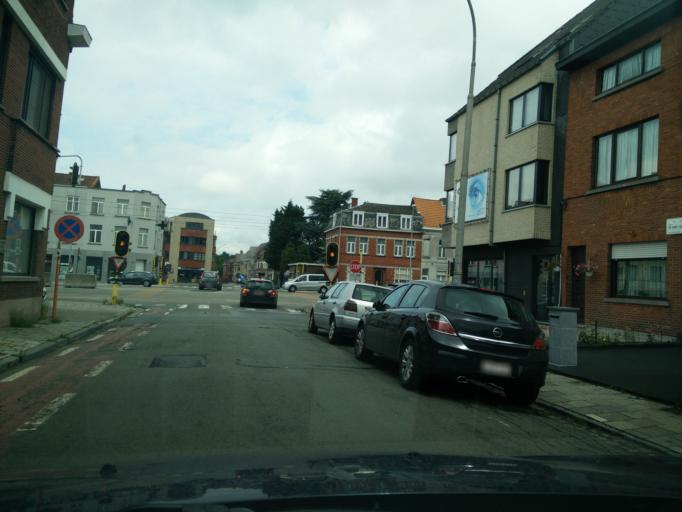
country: BE
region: Flanders
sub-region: Provincie Oost-Vlaanderen
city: Ledeberg
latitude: 51.0313
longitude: 3.7605
